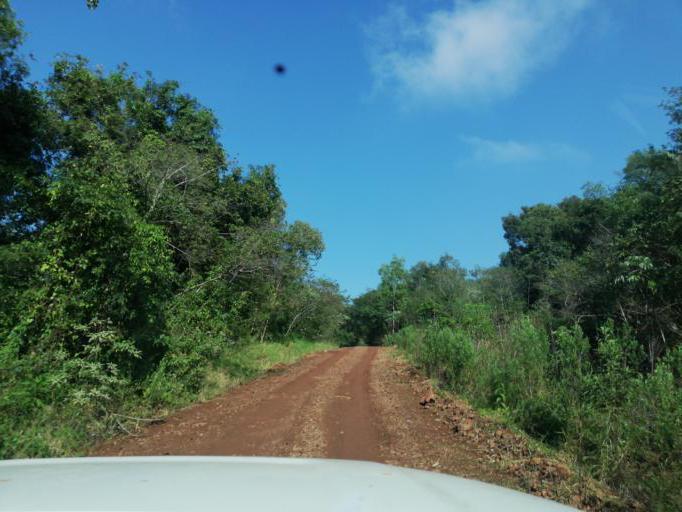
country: AR
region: Misiones
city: Cerro Azul
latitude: -27.6189
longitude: -55.5244
